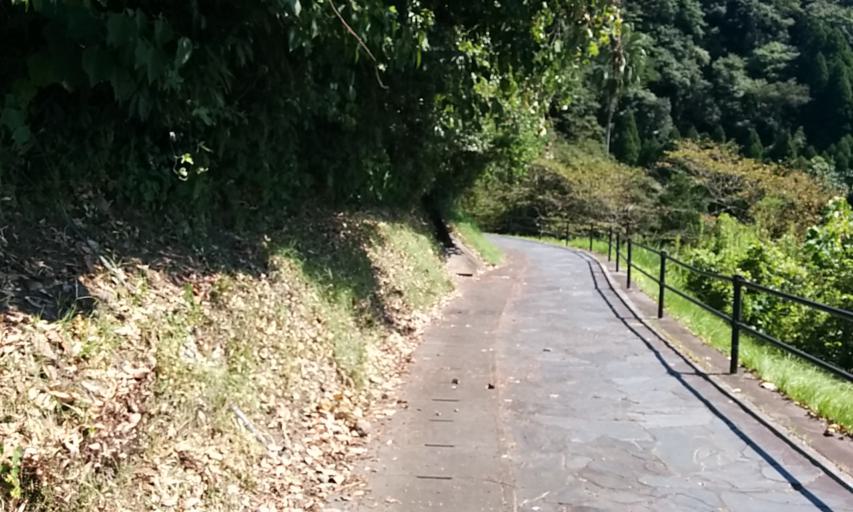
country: JP
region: Kagoshima
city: Kajiki
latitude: 31.7526
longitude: 130.6670
